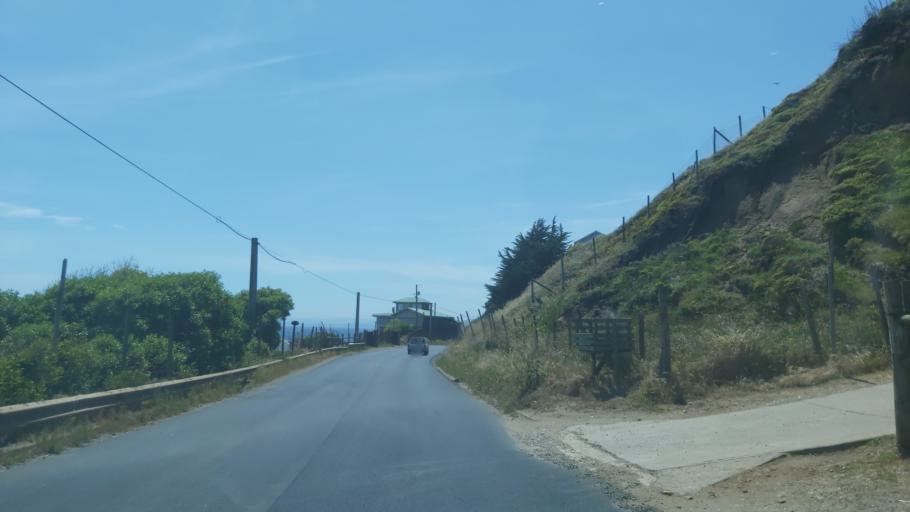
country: CL
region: Maule
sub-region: Provincia de Cauquenes
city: Cauquenes
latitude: -35.8317
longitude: -72.6201
